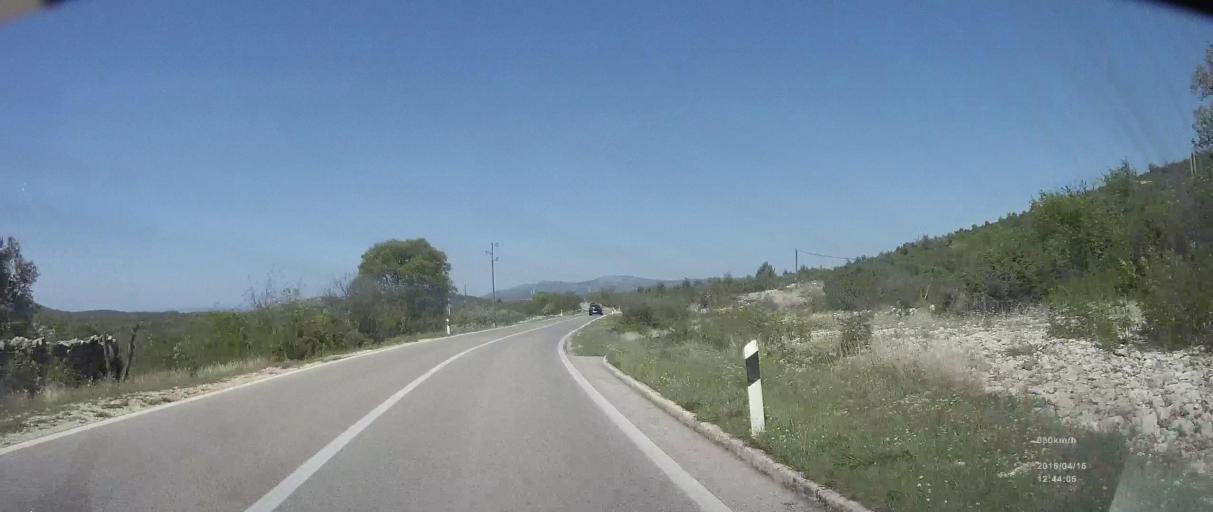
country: HR
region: Sibensko-Kniniska
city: Rogoznica
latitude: 43.6377
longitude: 16.0677
